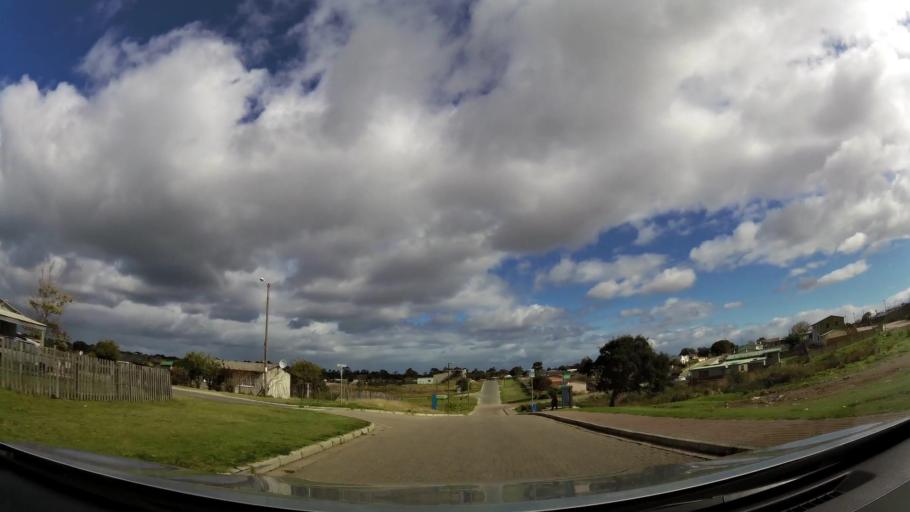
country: ZA
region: Western Cape
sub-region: Eden District Municipality
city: George
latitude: -34.0235
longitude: 22.4694
